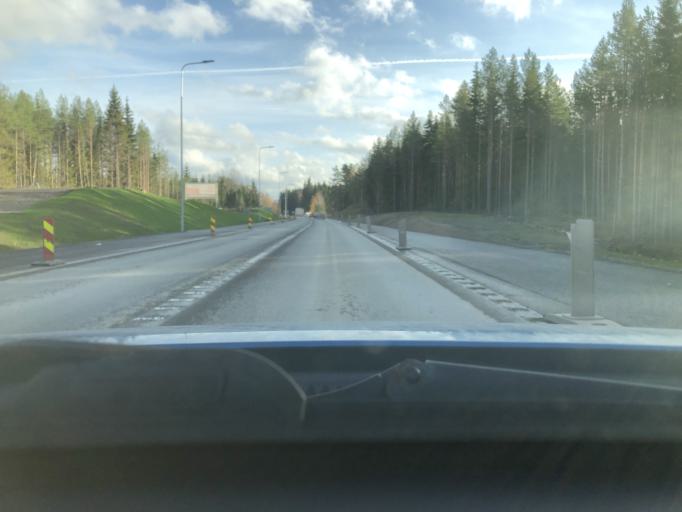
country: FI
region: Pirkanmaa
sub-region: Tampere
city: Kangasala
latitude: 61.4877
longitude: 23.9544
